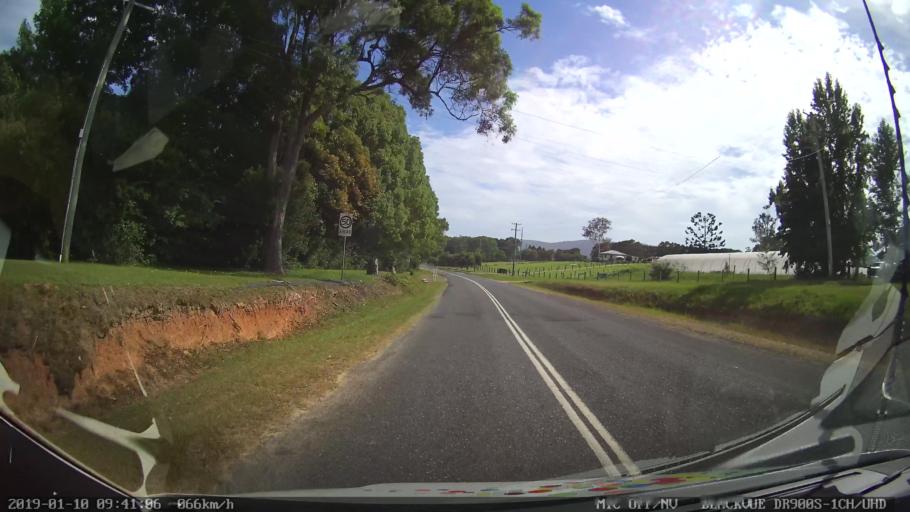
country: AU
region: New South Wales
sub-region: Coffs Harbour
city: Nana Glen
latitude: -30.1448
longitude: 153.0072
